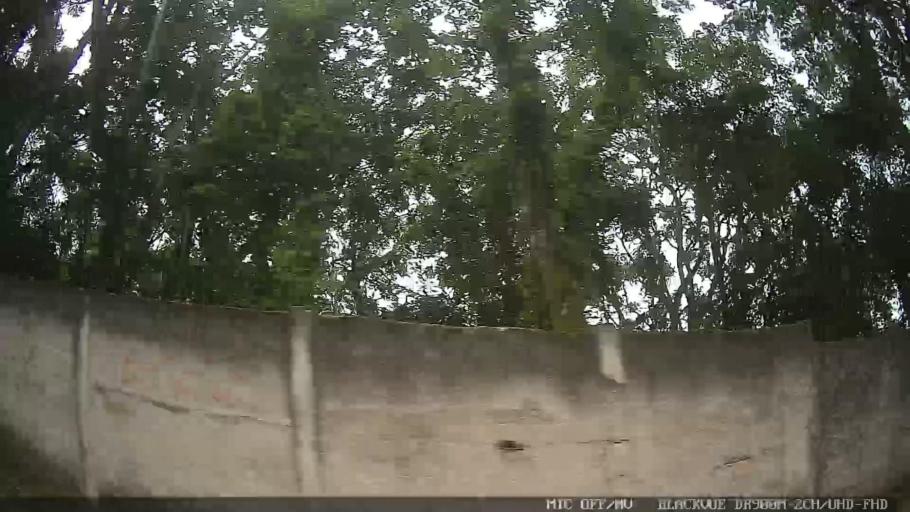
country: BR
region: Sao Paulo
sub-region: Aruja
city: Aruja
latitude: -23.4361
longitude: -46.2743
